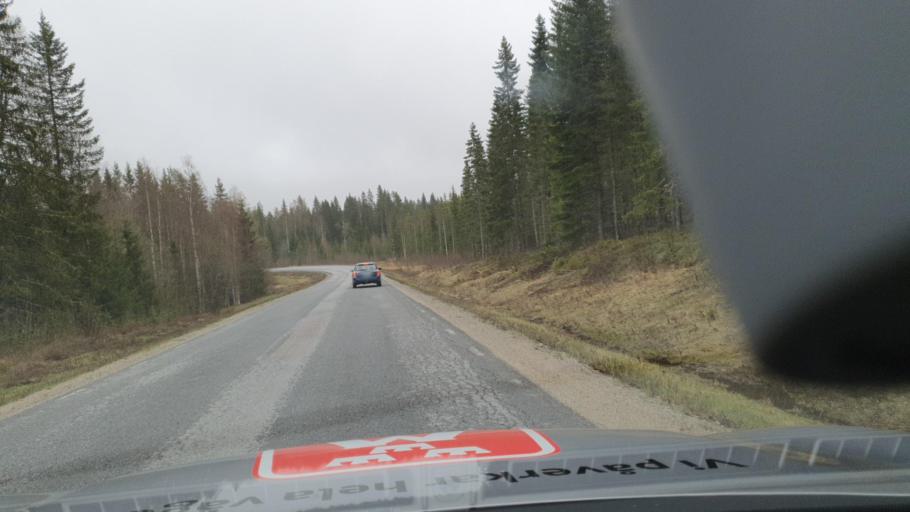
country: SE
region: Vaesternorrland
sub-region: OErnskoeldsviks Kommun
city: Husum
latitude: 63.4758
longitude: 19.2297
